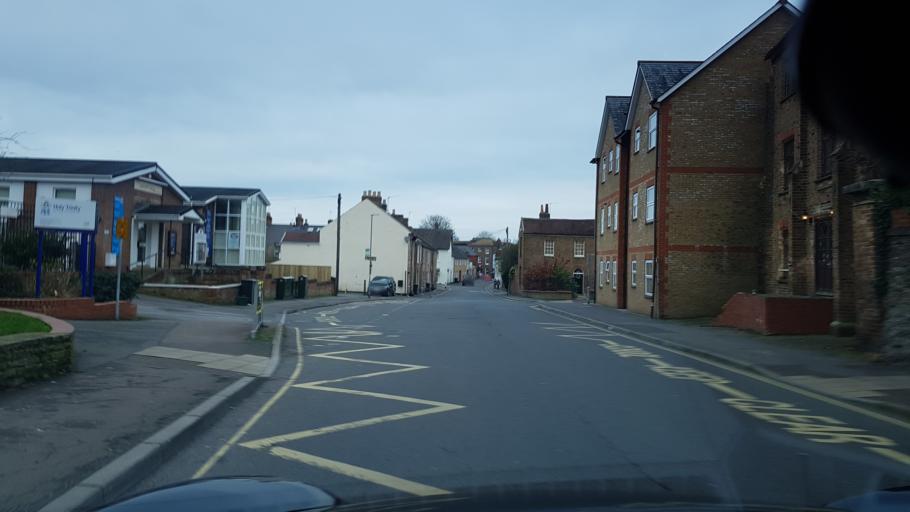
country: GB
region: England
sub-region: Somerset
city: Taunton
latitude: 51.0139
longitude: -3.0930
